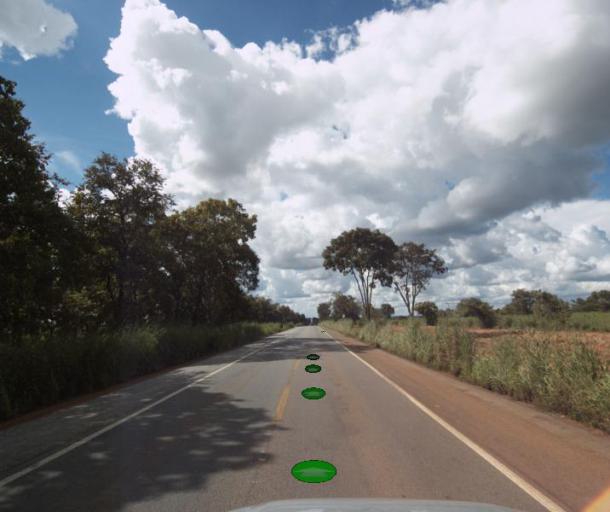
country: BR
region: Goias
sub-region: Porangatu
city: Porangatu
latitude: -13.3829
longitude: -49.1277
